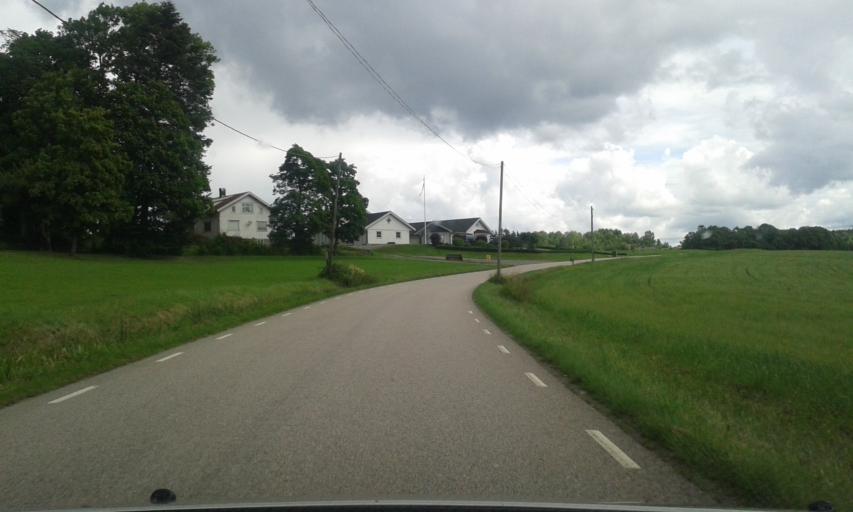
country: SE
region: Vaestra Goetaland
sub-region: Kungalvs Kommun
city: Kode
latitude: 57.9417
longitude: 11.8912
